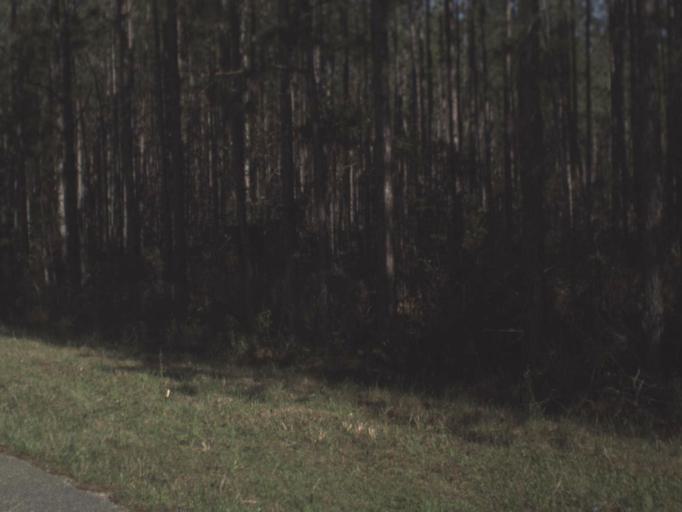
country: US
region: Florida
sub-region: Gulf County
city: Port Saint Joe
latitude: 29.8603
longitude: -85.2453
